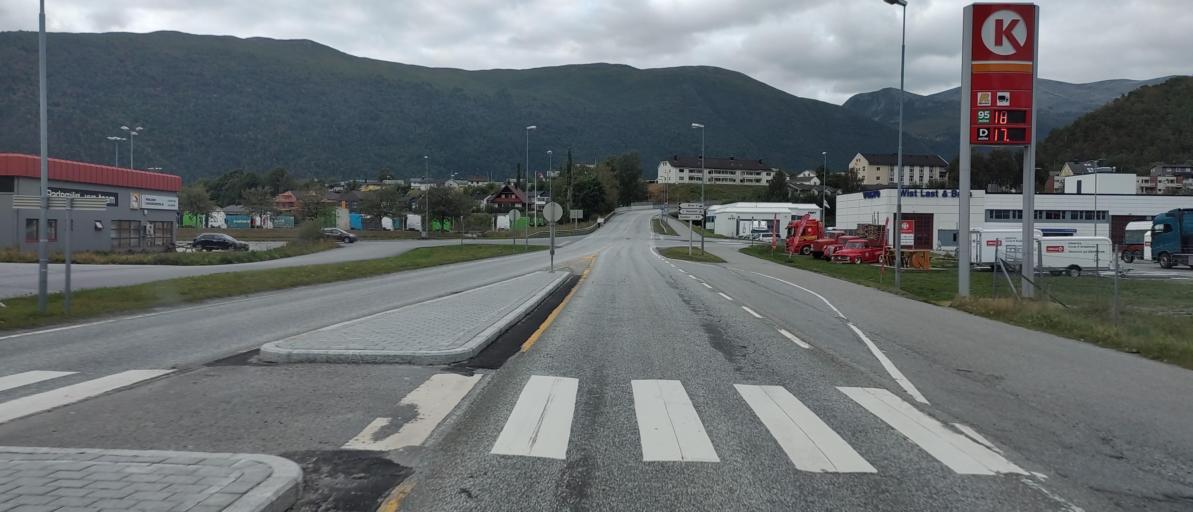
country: NO
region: More og Romsdal
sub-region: Rauma
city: Andalsnes
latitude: 62.5592
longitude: 7.6835
